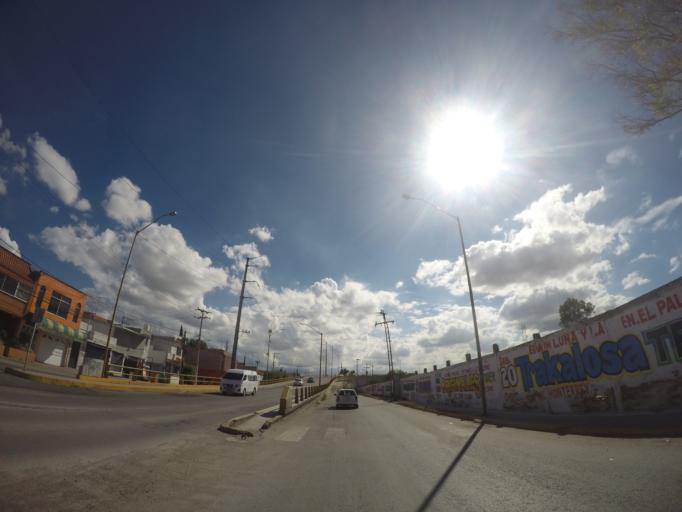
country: MX
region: San Luis Potosi
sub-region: San Luis Potosi
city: San Luis Potosi
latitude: 22.1589
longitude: -100.9666
